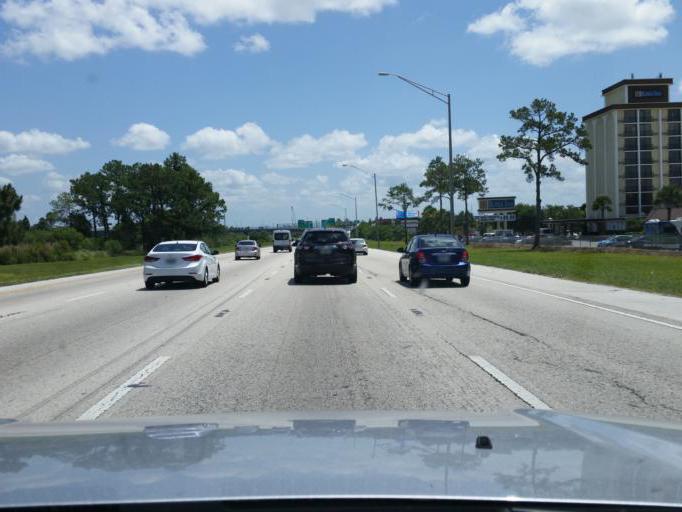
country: US
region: Florida
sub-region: Orange County
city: Doctor Phillips
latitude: 28.4605
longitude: -81.4709
